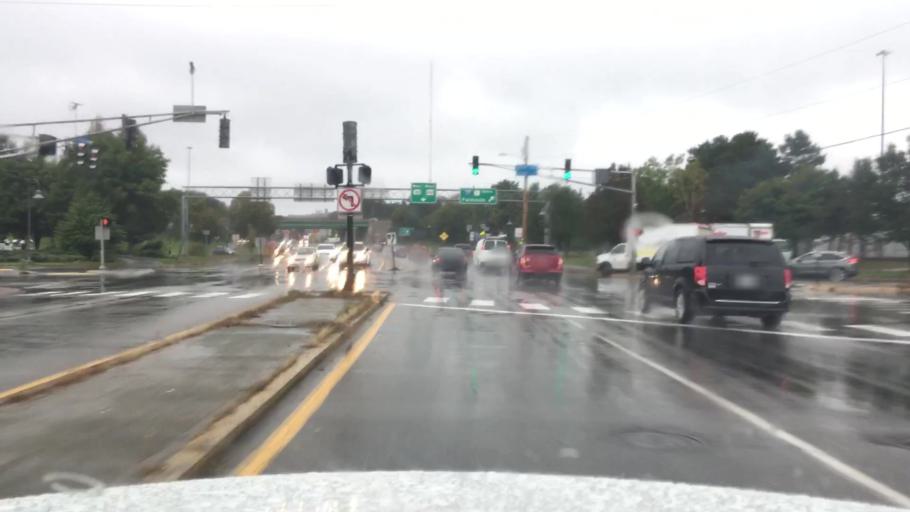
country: US
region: Maine
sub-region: Cumberland County
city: Portland
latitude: 43.6599
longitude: -70.2680
